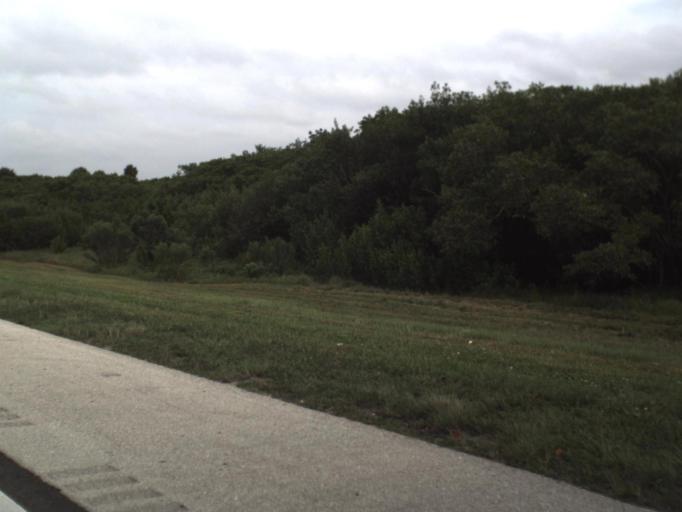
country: US
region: Florida
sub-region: Manatee County
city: Ellenton
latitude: 27.5125
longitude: -82.5008
